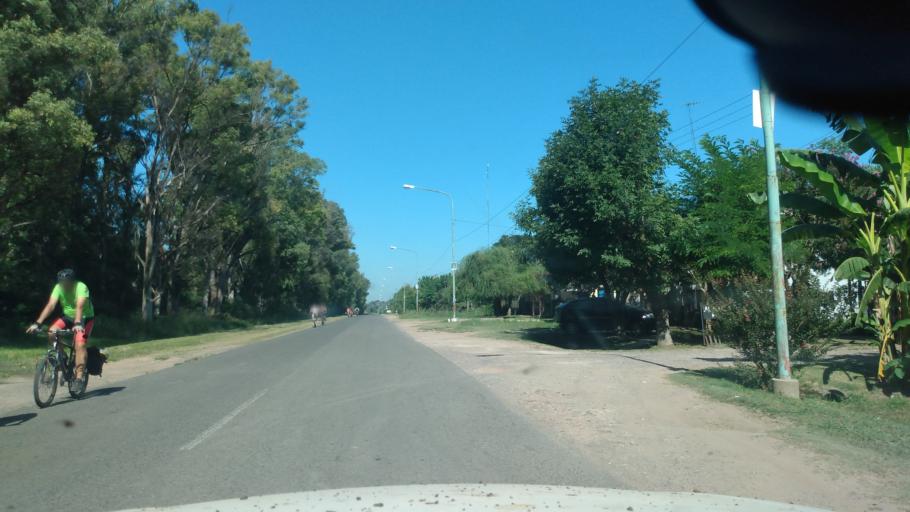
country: AR
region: Buenos Aires
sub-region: Partido de Lujan
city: Lujan
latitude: -34.5042
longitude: -59.0755
